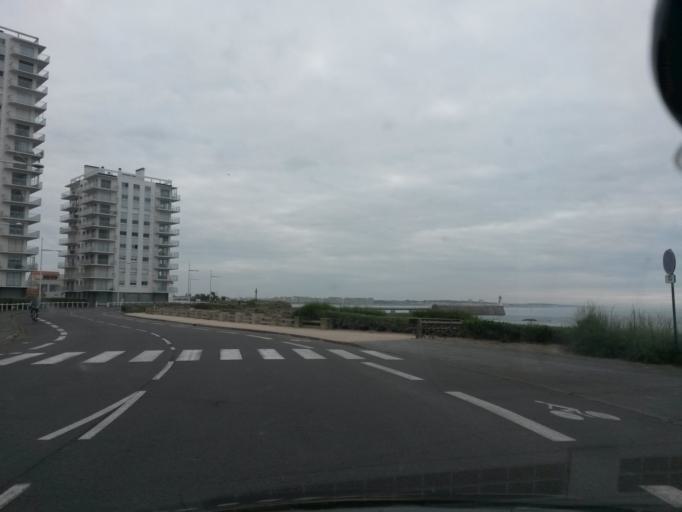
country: FR
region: Pays de la Loire
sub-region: Departement de la Vendee
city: Les Sables-d'Olonne
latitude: 46.4894
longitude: -1.7989
